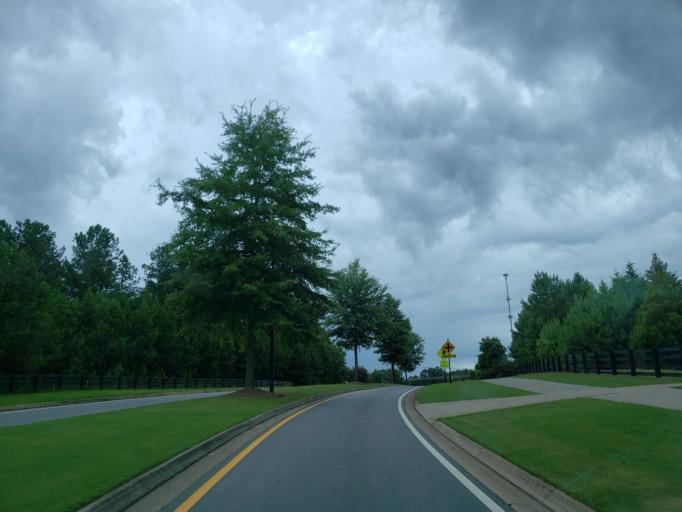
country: US
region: Georgia
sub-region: Paulding County
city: Dallas
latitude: 34.0134
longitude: -84.7998
